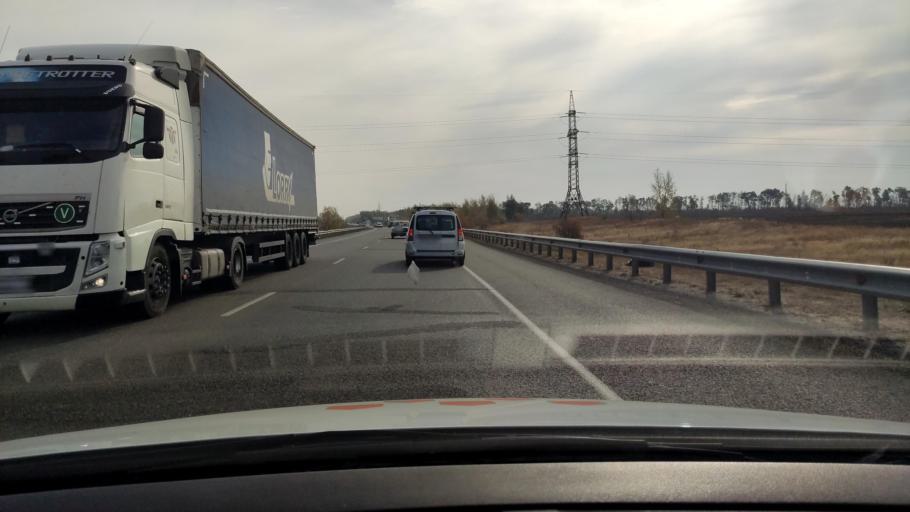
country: RU
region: Voronezj
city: Novaya Usman'
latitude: 51.6975
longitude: 39.4336
